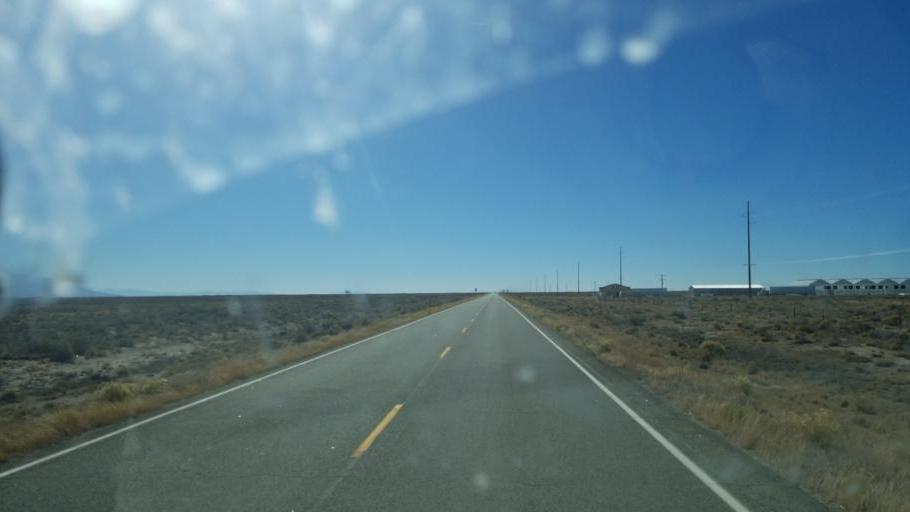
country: US
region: Colorado
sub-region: Saguache County
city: Saguache
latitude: 37.9521
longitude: -105.9034
